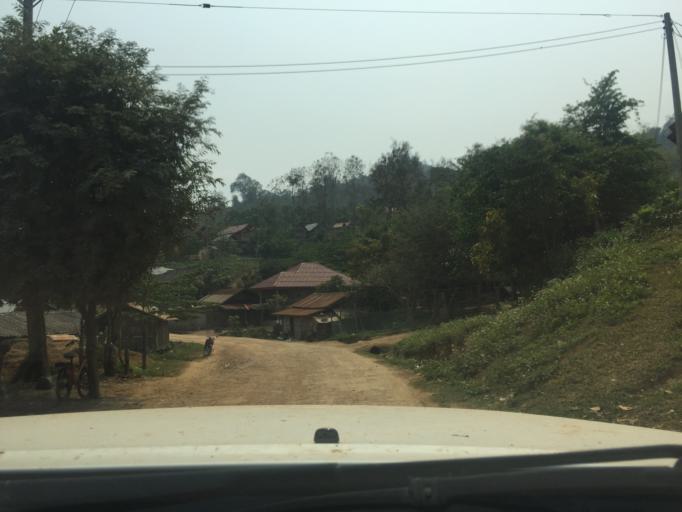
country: LA
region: Loungnamtha
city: Muang Nale
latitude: 20.3025
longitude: 101.6471
